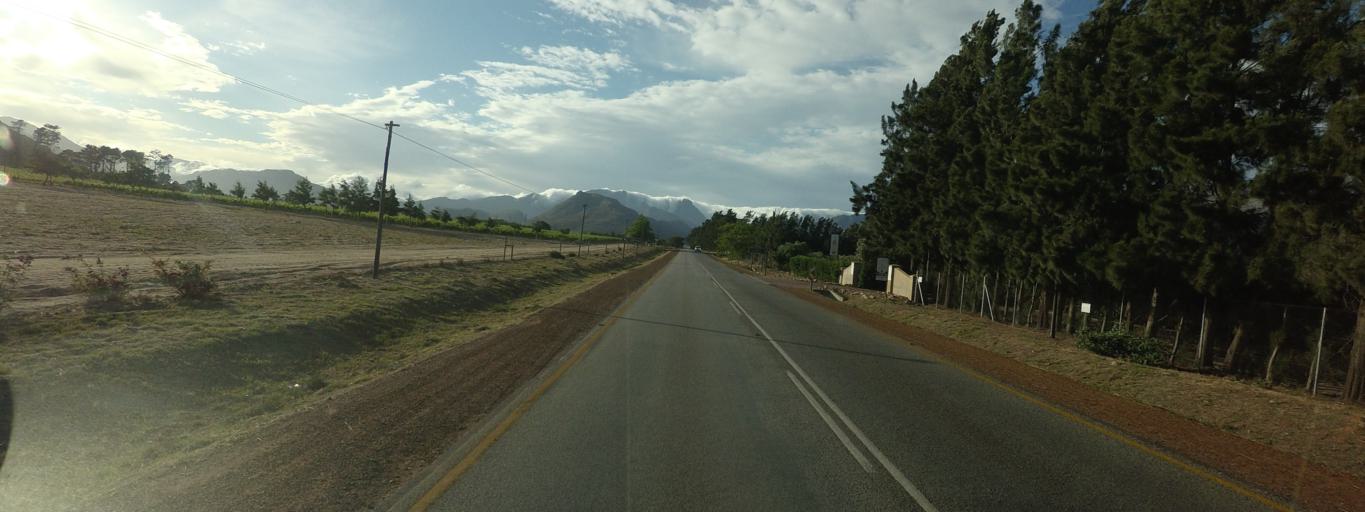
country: ZA
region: Western Cape
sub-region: Cape Winelands District Municipality
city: Paarl
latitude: -33.8648
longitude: 19.0404
